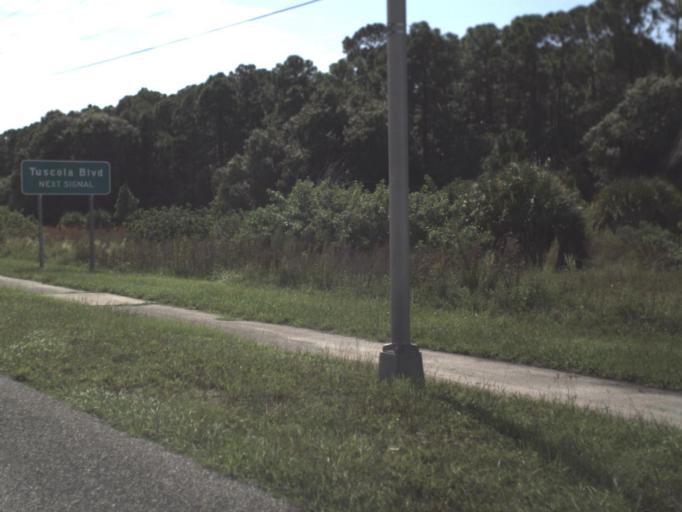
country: US
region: Florida
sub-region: Sarasota County
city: North Port
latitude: 27.0414
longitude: -82.2297
